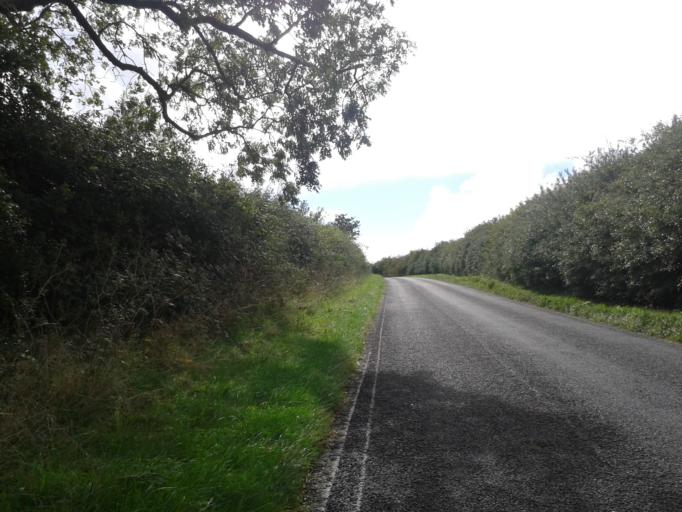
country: GB
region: England
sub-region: Cambridgeshire
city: Duxford
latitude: 52.0547
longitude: 0.1532
